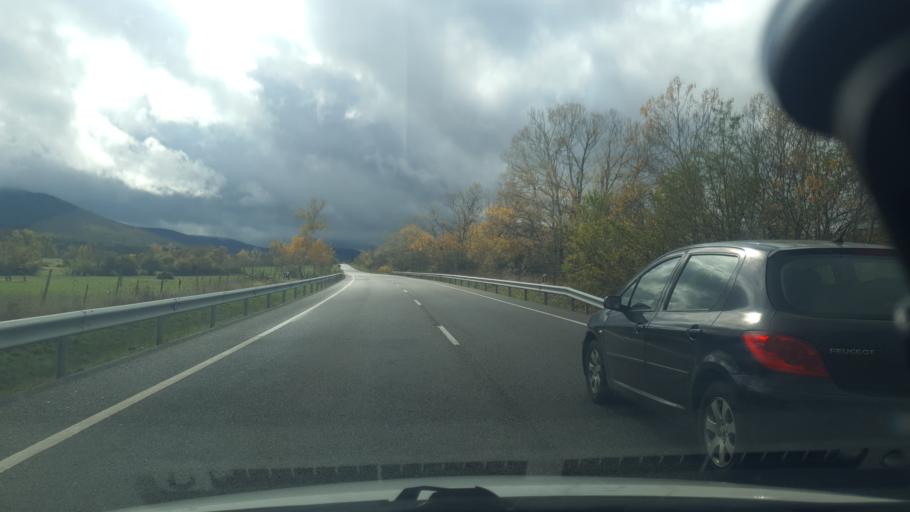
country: ES
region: Castille and Leon
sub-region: Provincia de Segovia
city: Collado Hermoso
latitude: 41.0496
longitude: -3.9100
